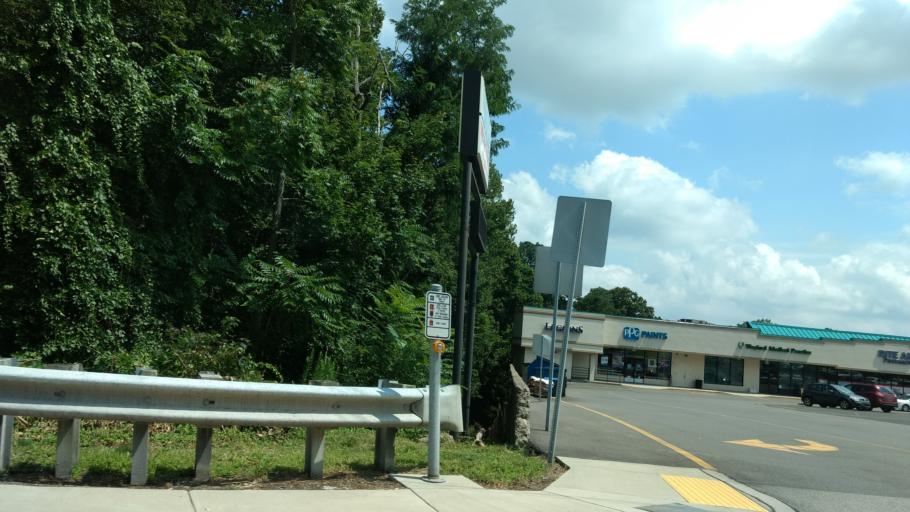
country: US
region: Pennsylvania
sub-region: Allegheny County
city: West View
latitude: 40.5487
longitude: -80.0370
